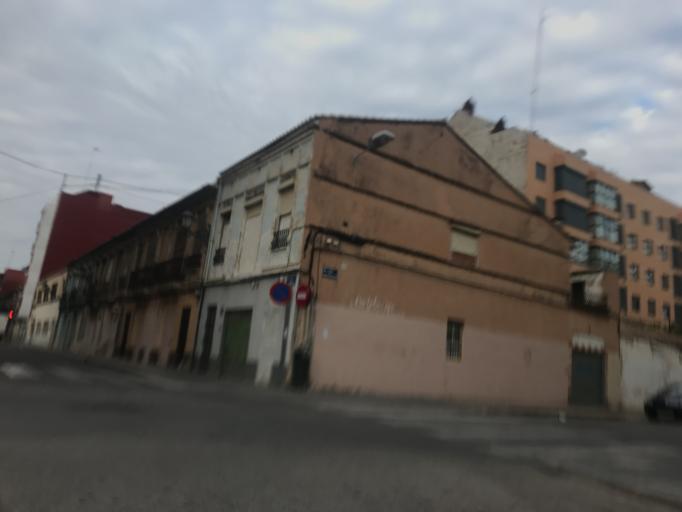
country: ES
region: Valencia
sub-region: Provincia de Valencia
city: Valencia
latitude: 39.4664
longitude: -0.3438
